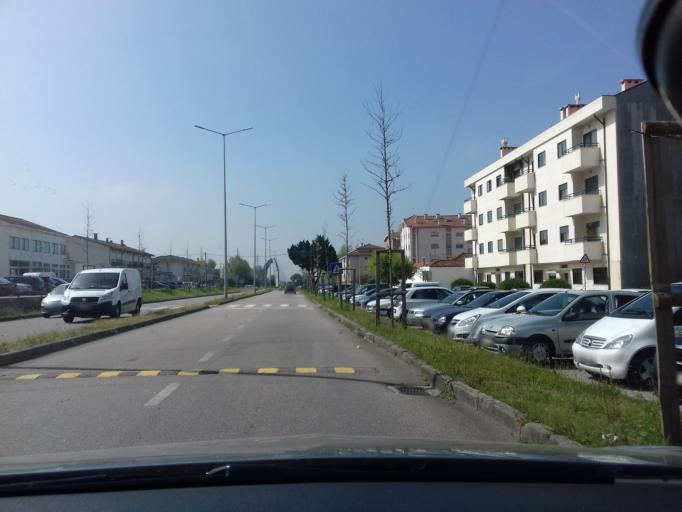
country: PT
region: Aveiro
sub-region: Espinho
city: Espinho
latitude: 41.0056
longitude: -8.6343
